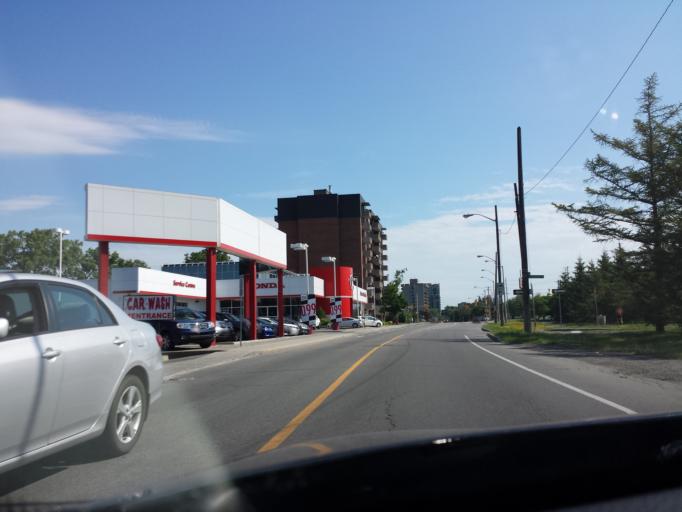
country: CA
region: Ontario
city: Bells Corners
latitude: 45.3760
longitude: -75.7766
